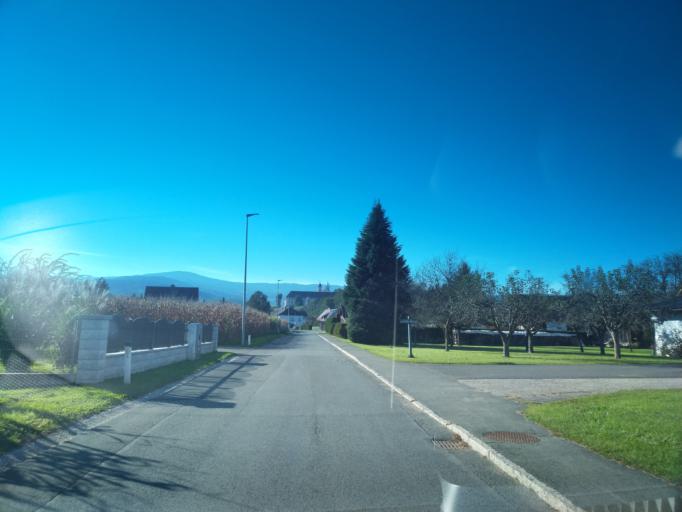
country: AT
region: Styria
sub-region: Politischer Bezirk Deutschlandsberg
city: Stainz
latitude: 46.8942
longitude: 15.2750
